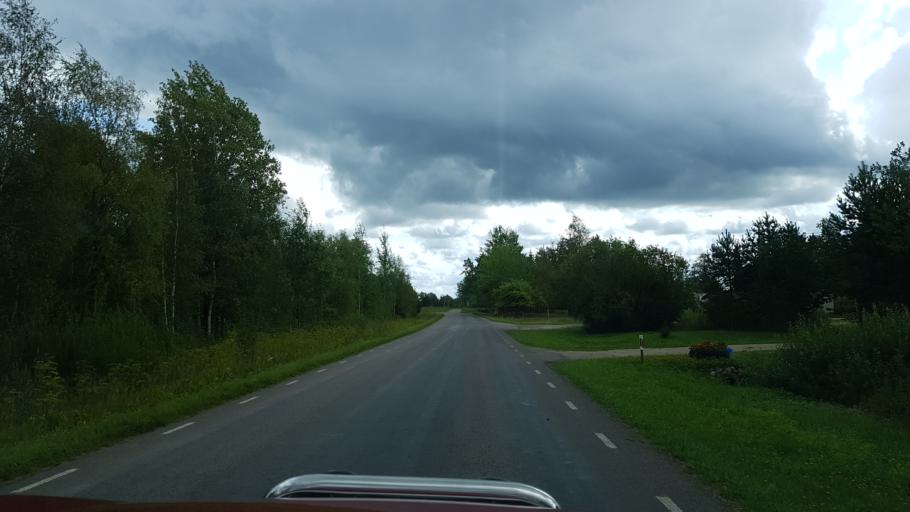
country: EE
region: Laeaene
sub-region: Lihula vald
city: Lihula
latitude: 58.7232
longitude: 23.9569
